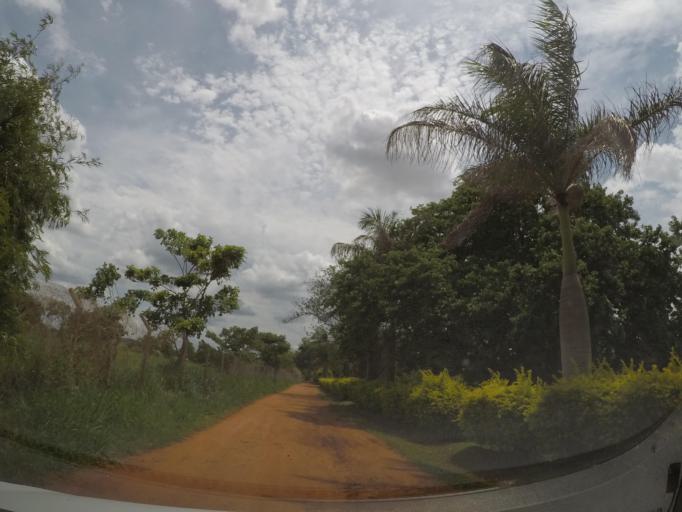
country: BR
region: Sao Paulo
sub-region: Sumare
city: Sumare
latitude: -22.8507
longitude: -47.3001
